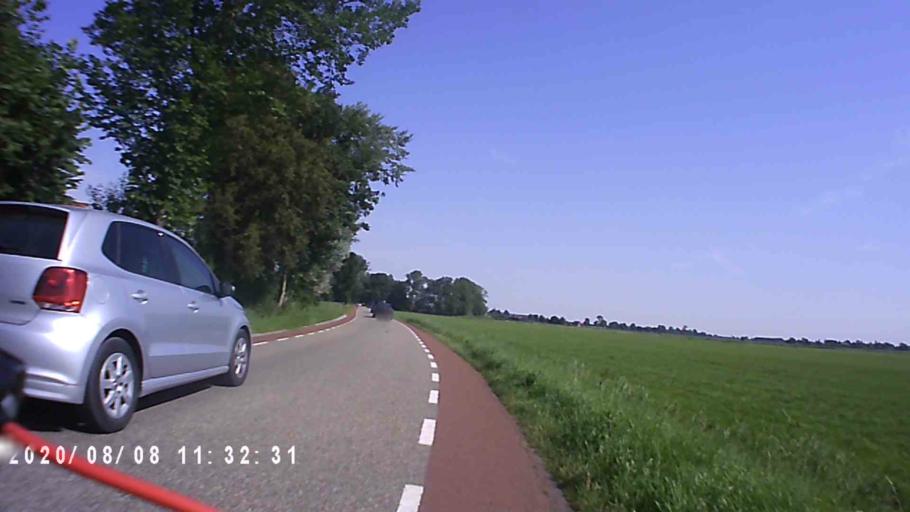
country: NL
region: Groningen
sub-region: Gemeente Zuidhorn
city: Zuidhorn
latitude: 53.2091
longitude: 6.3888
